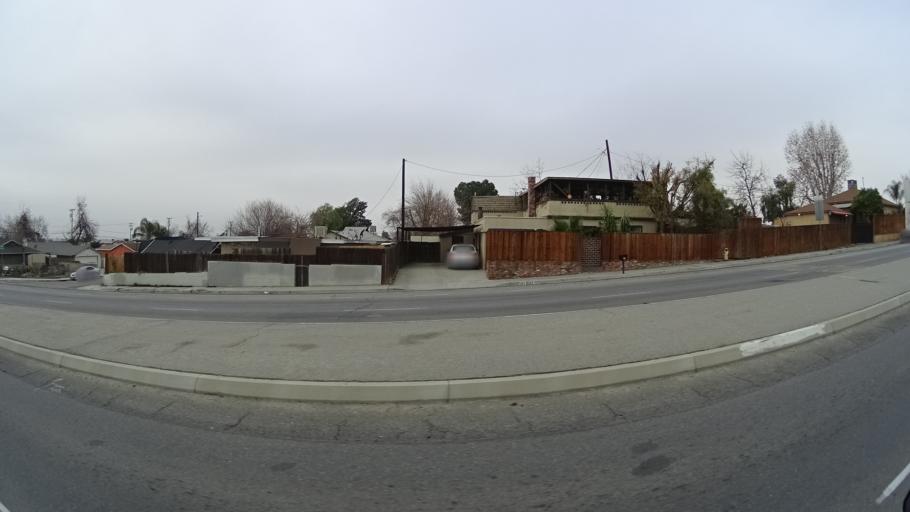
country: US
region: California
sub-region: Kern County
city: Bakersfield
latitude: 35.3734
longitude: -118.9496
